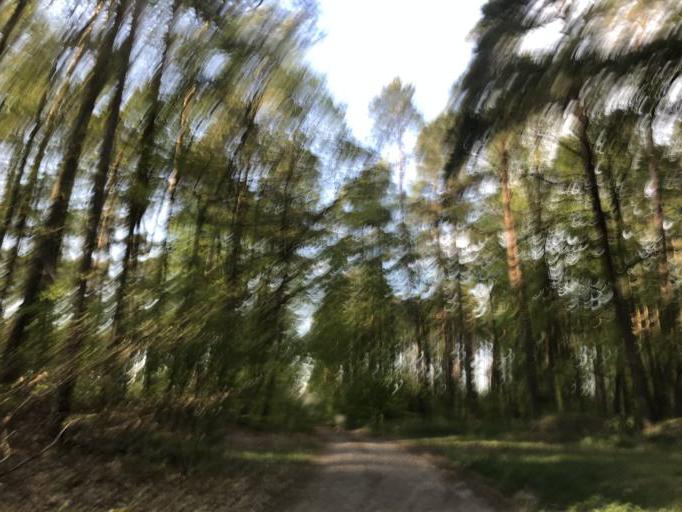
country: DE
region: Brandenburg
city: Joachimsthal
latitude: 52.9703
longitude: 13.7240
